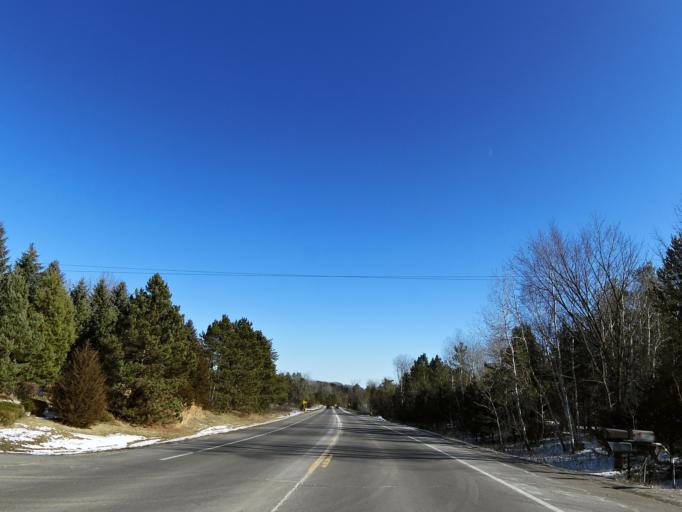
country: US
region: Minnesota
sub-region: Washington County
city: Stillwater
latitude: 45.0764
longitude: -92.8226
